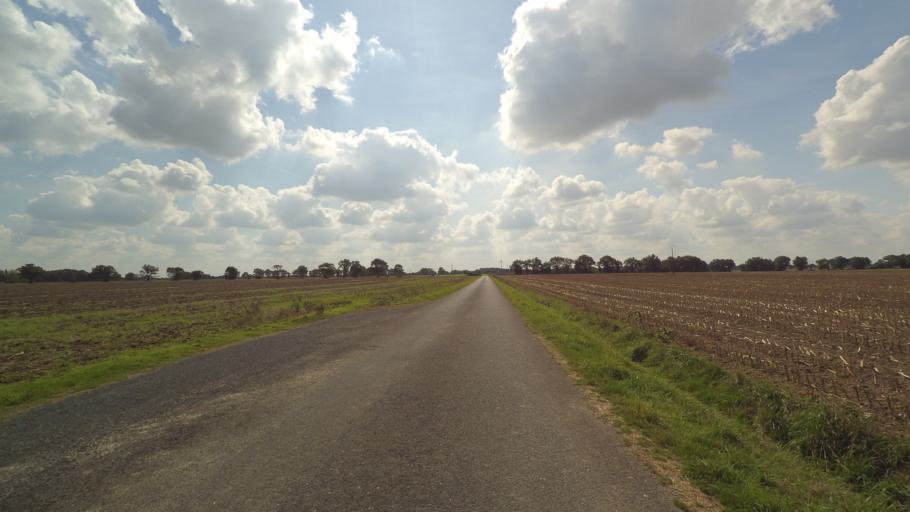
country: FR
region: Pays de la Loire
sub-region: Departement de la Vendee
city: Bouffere
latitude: 46.9691
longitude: -1.3778
